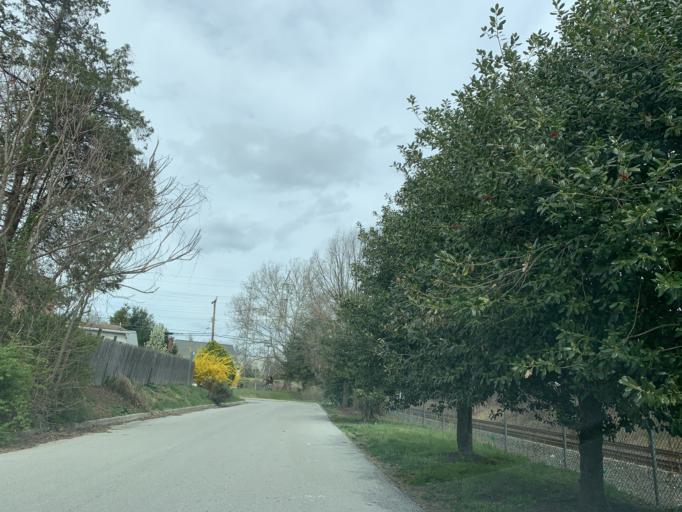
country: US
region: Maryland
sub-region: Baltimore County
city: Baltimore Highlands
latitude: 39.2268
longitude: -76.6387
